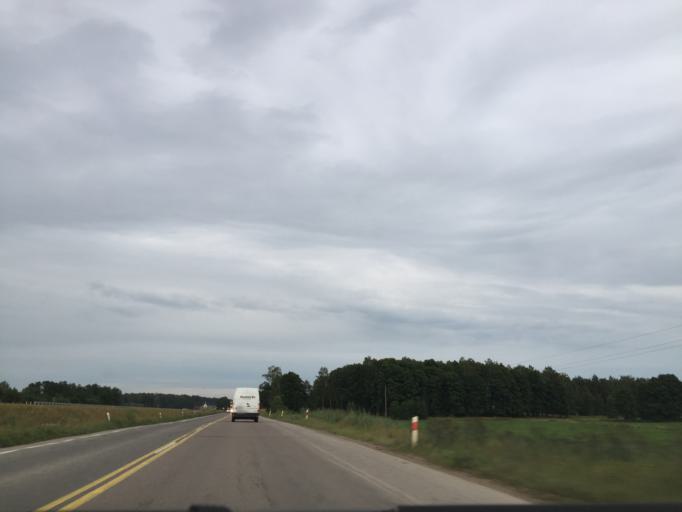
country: PL
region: Podlasie
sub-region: Powiat wysokomazowiecki
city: Sokoly
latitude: 53.1216
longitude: 22.6593
